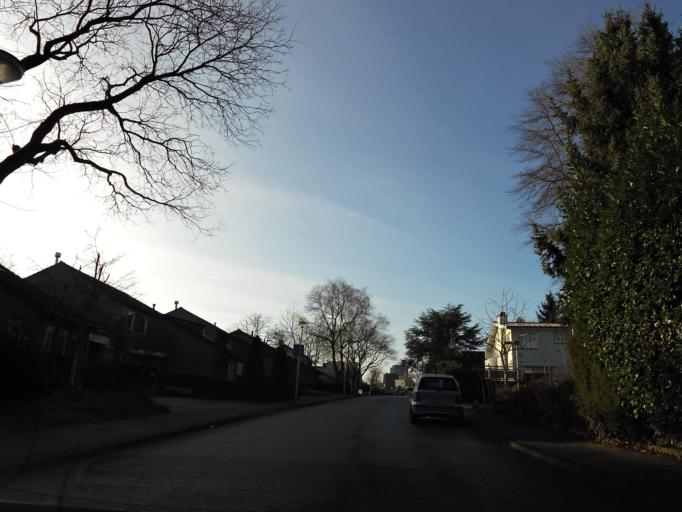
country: NL
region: Limburg
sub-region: Gemeente Heerlen
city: Heerlen
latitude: 50.8771
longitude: 5.9961
